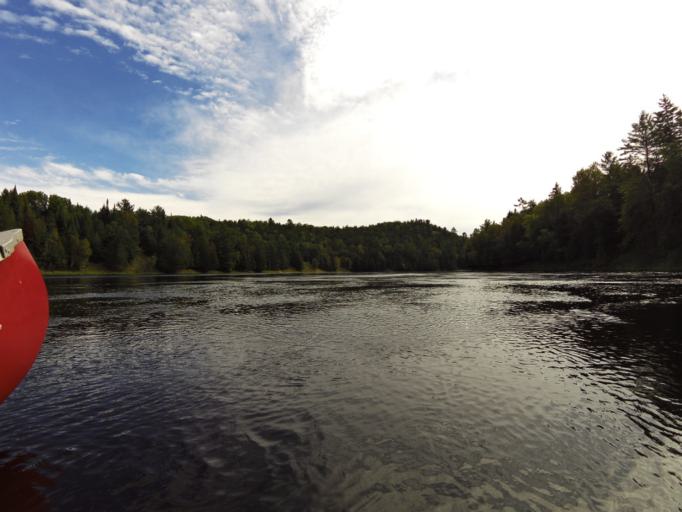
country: CA
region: Quebec
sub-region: Outaouais
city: Wakefield
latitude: 45.7719
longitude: -75.9388
